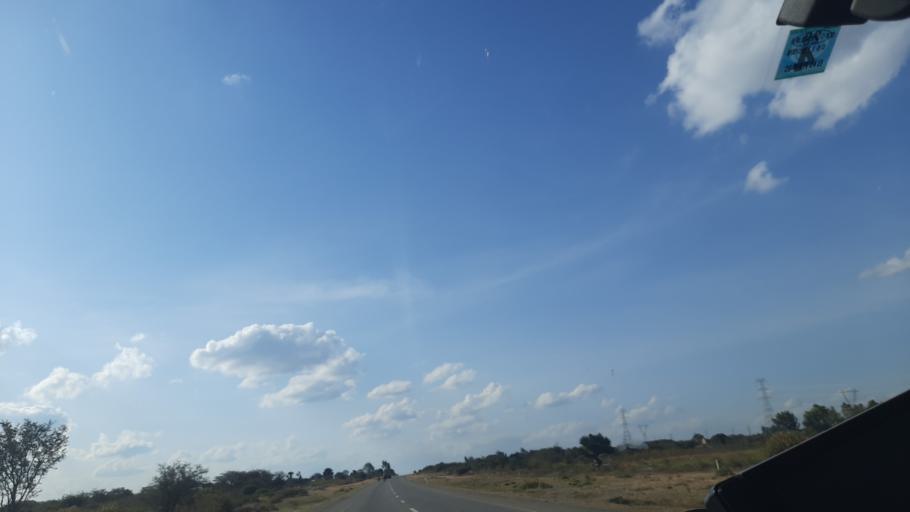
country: TZ
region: Singida
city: Puma
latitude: -5.0372
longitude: 34.7592
